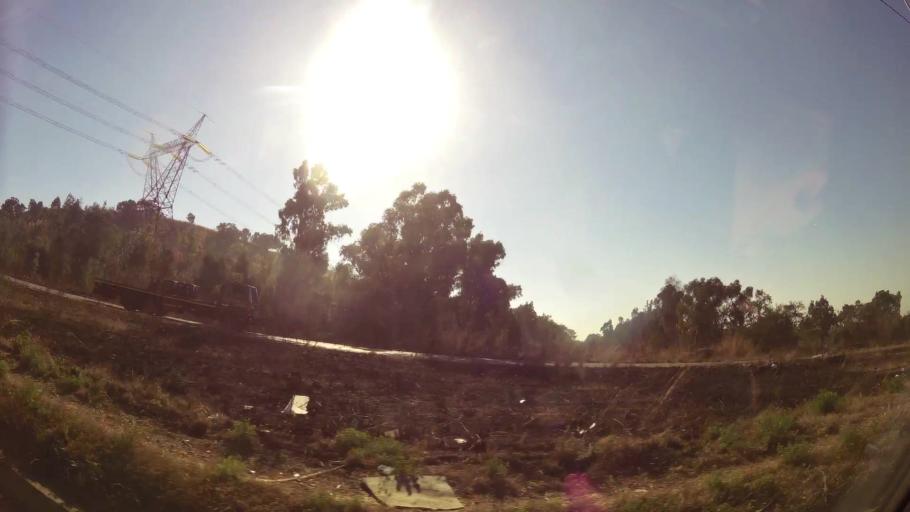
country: ZA
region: Gauteng
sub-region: City of Johannesburg Metropolitan Municipality
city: Johannesburg
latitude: -26.2350
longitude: 28.0956
